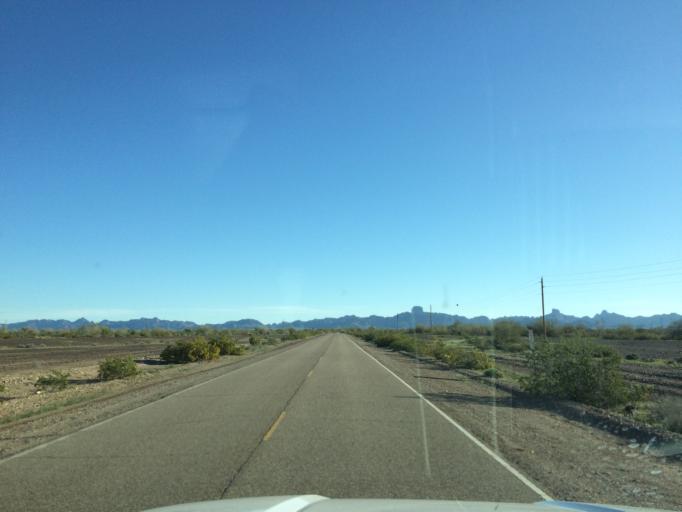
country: US
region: Arizona
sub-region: Yuma County
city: Wellton
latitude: 32.9793
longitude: -114.2744
